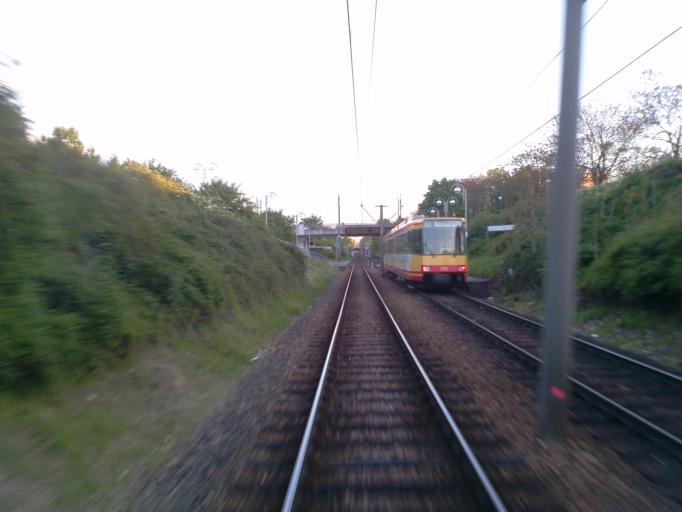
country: DE
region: Baden-Wuerttemberg
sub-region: Karlsruhe Region
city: Karlsruhe
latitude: 49.0252
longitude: 8.3758
